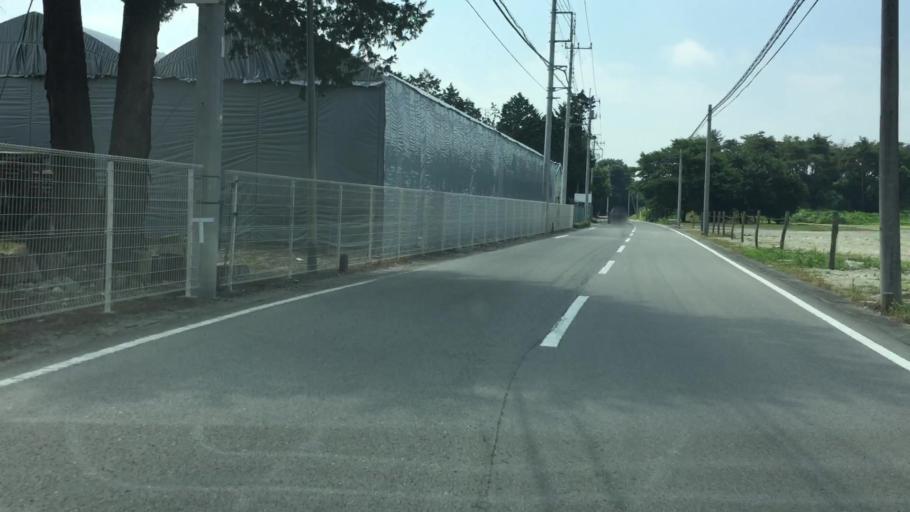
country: JP
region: Tochigi
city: Kuroiso
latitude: 36.9512
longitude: 139.9604
